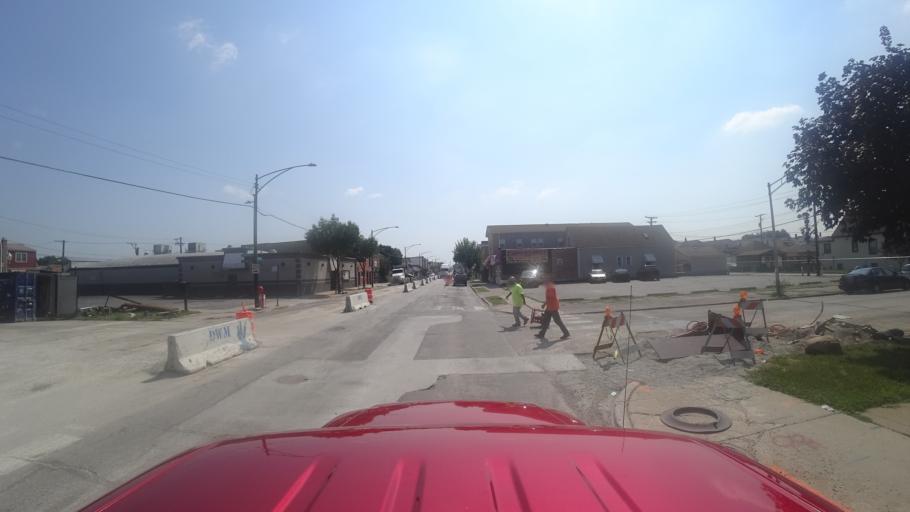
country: US
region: Illinois
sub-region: Cook County
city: Cicero
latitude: 41.8078
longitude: -87.7287
